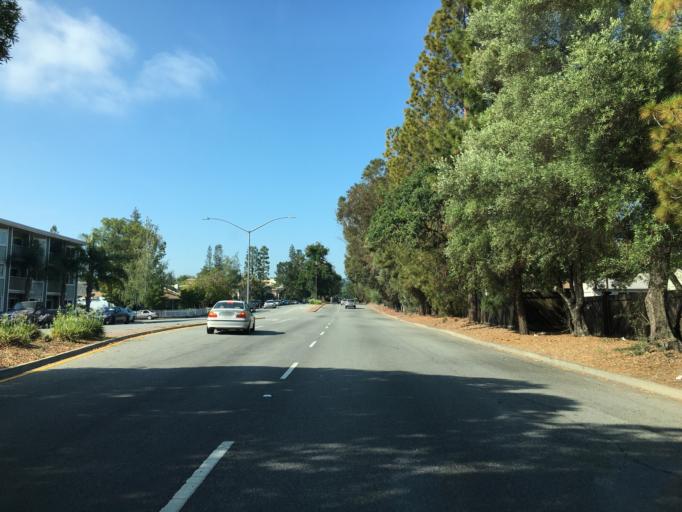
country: US
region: California
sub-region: San Mateo County
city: Woodside
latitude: 37.4523
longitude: -122.2300
